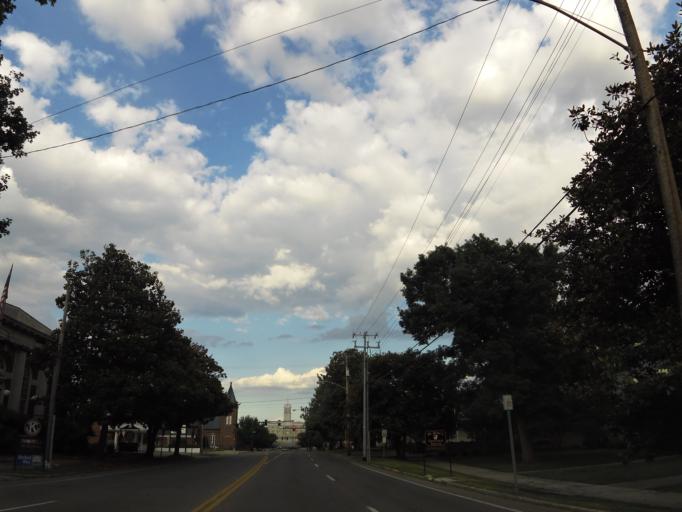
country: US
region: Tennessee
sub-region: Maury County
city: Columbia
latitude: 35.6154
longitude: -87.0386
